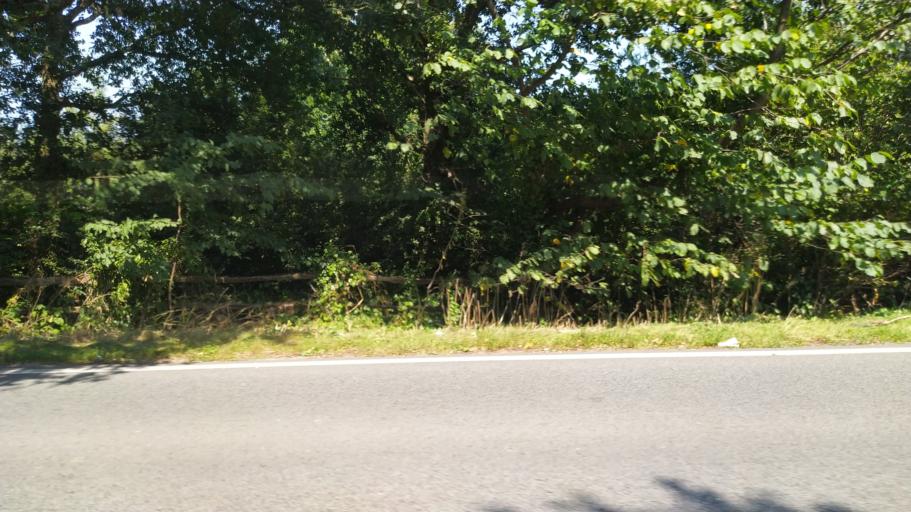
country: GB
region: England
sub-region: Hampshire
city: Totton
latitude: 50.9095
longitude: -1.4891
